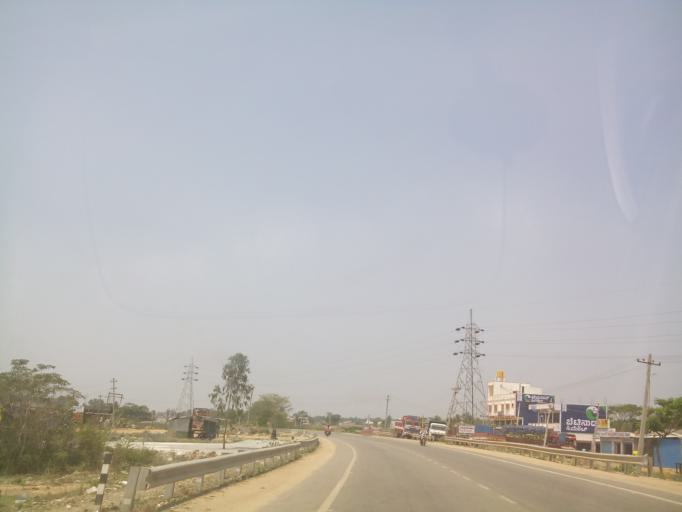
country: IN
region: Karnataka
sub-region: Hassan
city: Hassan
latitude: 12.9914
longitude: 76.0874
